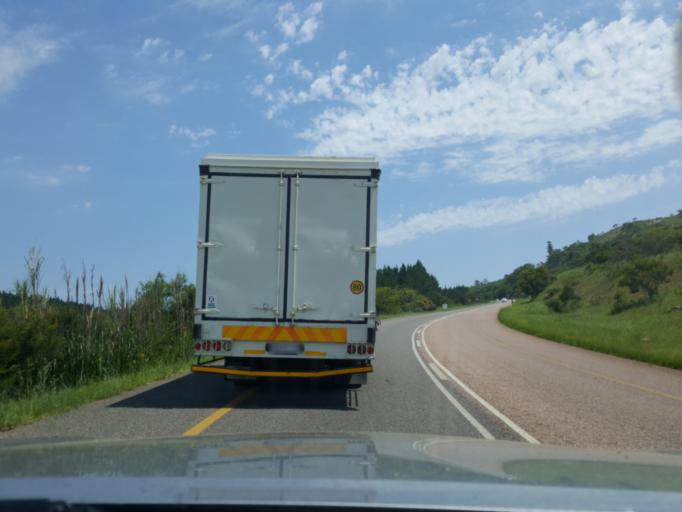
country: ZA
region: Mpumalanga
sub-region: Ehlanzeni District
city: White River
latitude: -25.1931
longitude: 31.0051
